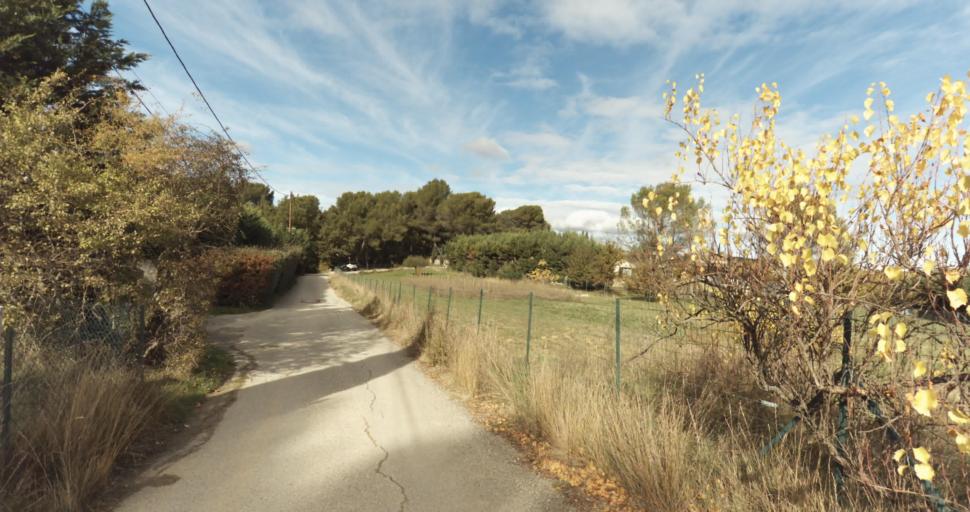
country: FR
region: Provence-Alpes-Cote d'Azur
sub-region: Departement des Bouches-du-Rhone
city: Venelles
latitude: 43.6106
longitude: 5.4929
